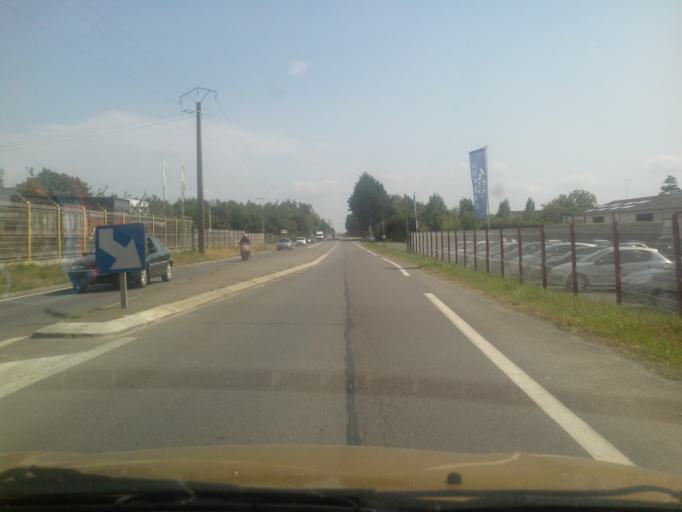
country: FR
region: Brittany
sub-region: Departement d'Ille-et-Vilaine
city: Melesse
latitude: 48.2286
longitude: -1.7059
